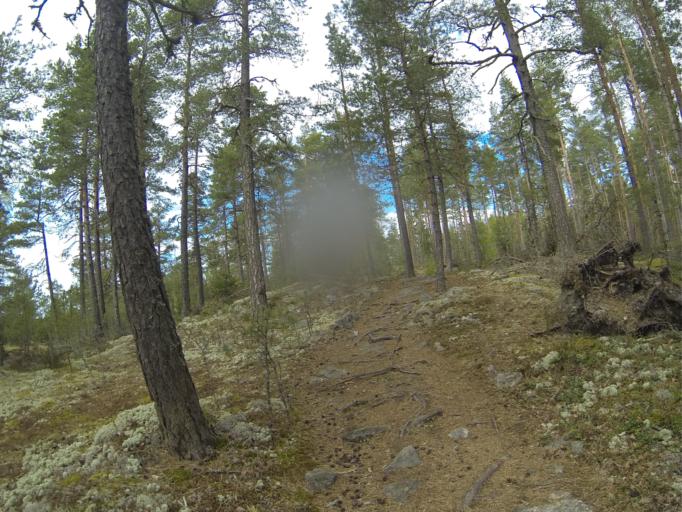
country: FI
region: Varsinais-Suomi
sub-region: Salo
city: Salo
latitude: 60.3507
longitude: 23.1104
